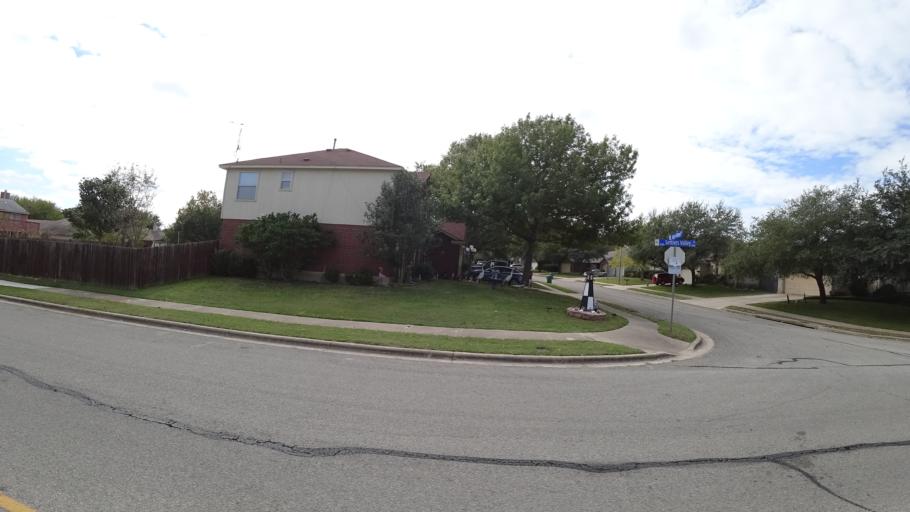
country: US
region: Texas
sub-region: Travis County
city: Pflugerville
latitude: 30.4386
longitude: -97.6321
